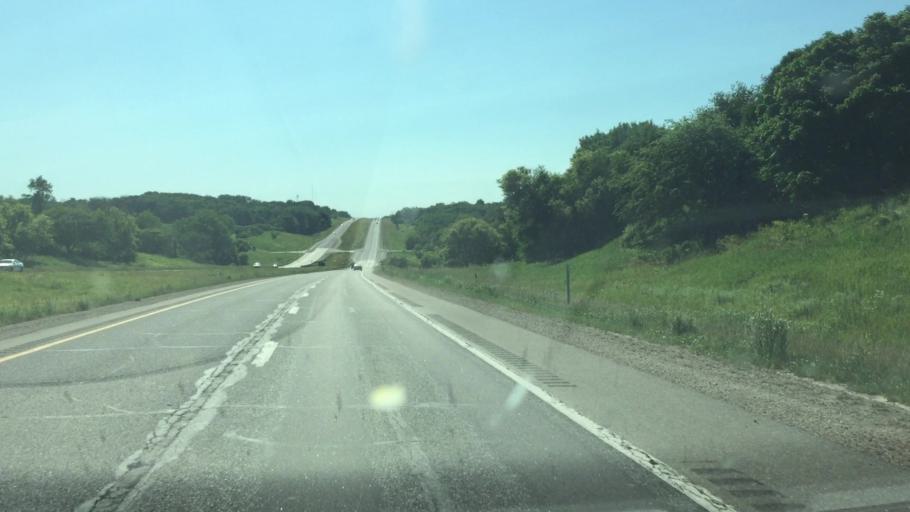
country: US
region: Iowa
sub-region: Linn County
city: Ely
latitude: 41.9254
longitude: -91.5722
